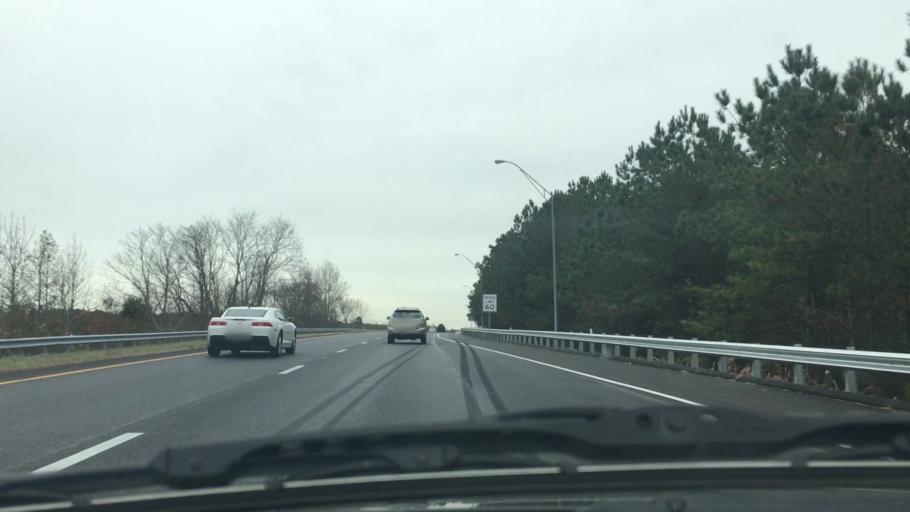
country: US
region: Virginia
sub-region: City of Portsmouth
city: Portsmouth Heights
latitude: 36.8718
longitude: -76.3723
